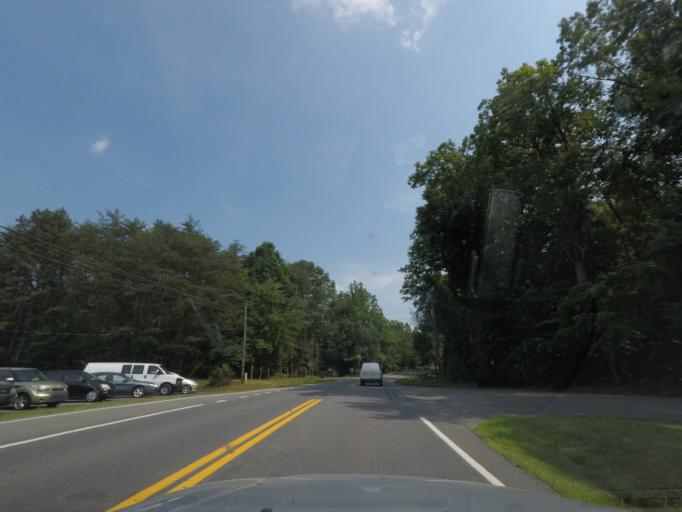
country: US
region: Virginia
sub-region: Fluvanna County
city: Palmyra
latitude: 37.8740
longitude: -78.2607
